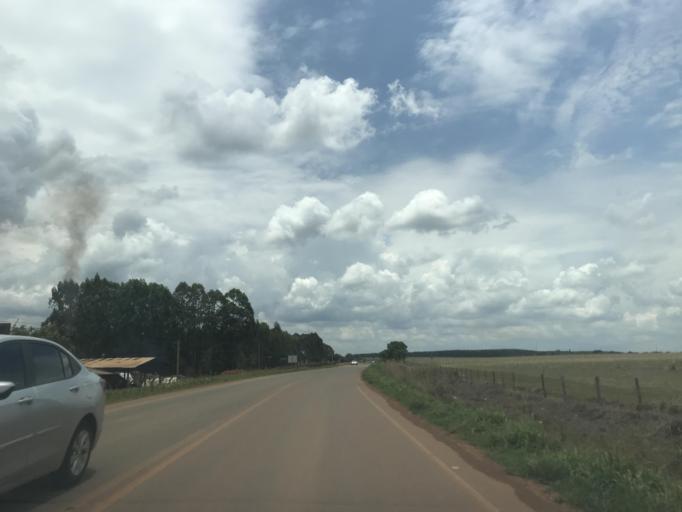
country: BR
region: Goias
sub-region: Vianopolis
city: Vianopolis
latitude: -16.7416
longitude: -48.4724
